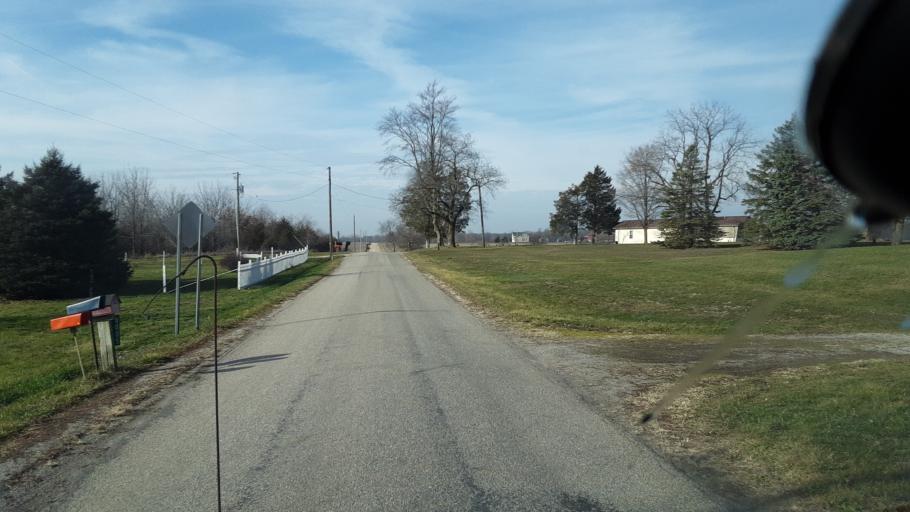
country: US
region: Ohio
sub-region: Defiance County
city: Hicksville
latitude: 41.2709
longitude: -84.8080
